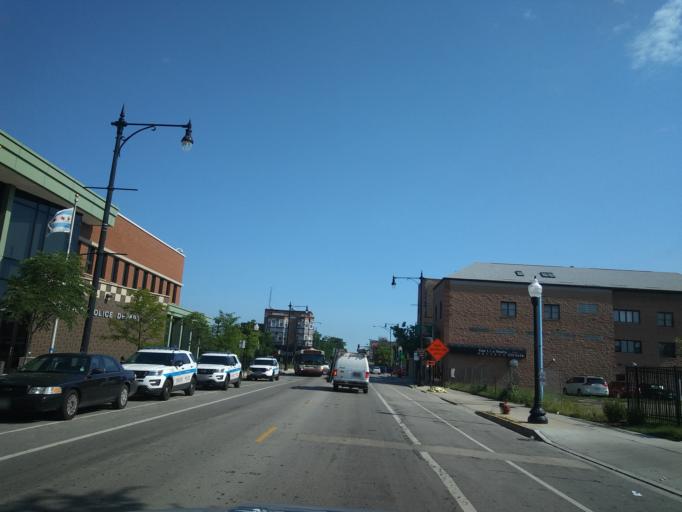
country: US
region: Illinois
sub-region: Cook County
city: Chicago
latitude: 41.8369
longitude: -87.6462
